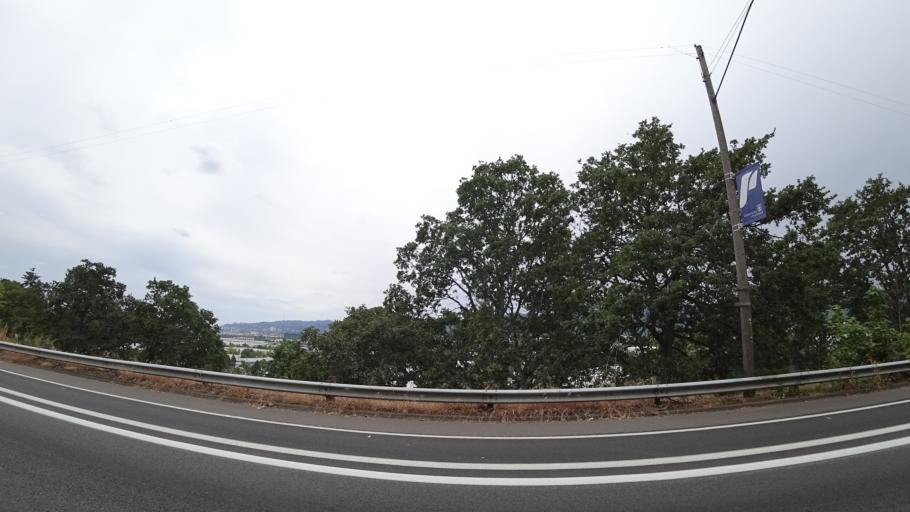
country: US
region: Oregon
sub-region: Multnomah County
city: Portland
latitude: 45.5740
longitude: -122.7042
